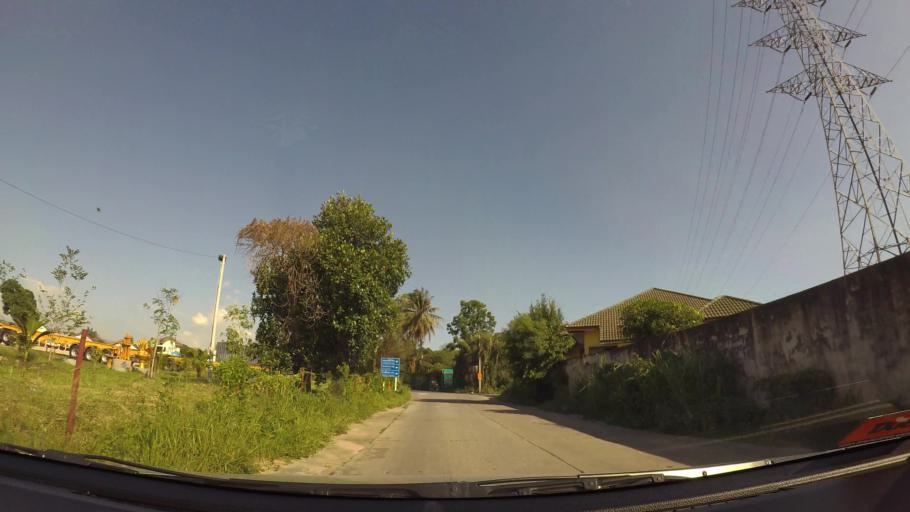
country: TH
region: Chon Buri
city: Si Racha
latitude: 13.1479
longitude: 100.9419
